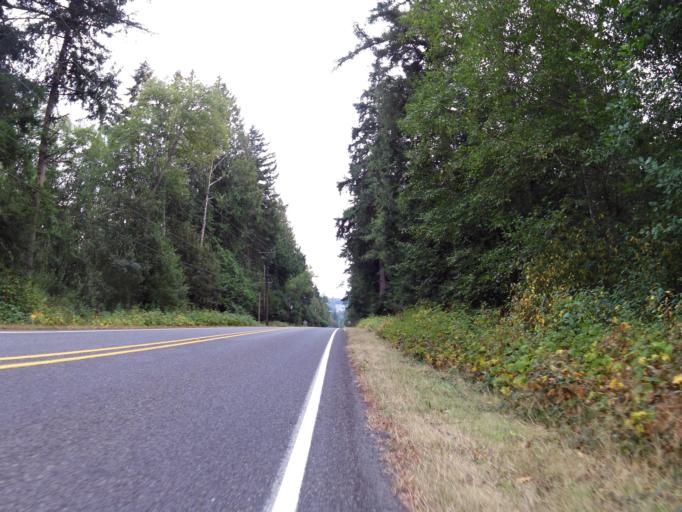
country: US
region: Washington
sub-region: Jefferson County
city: Port Ludlow
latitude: 47.9658
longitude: -122.6977
